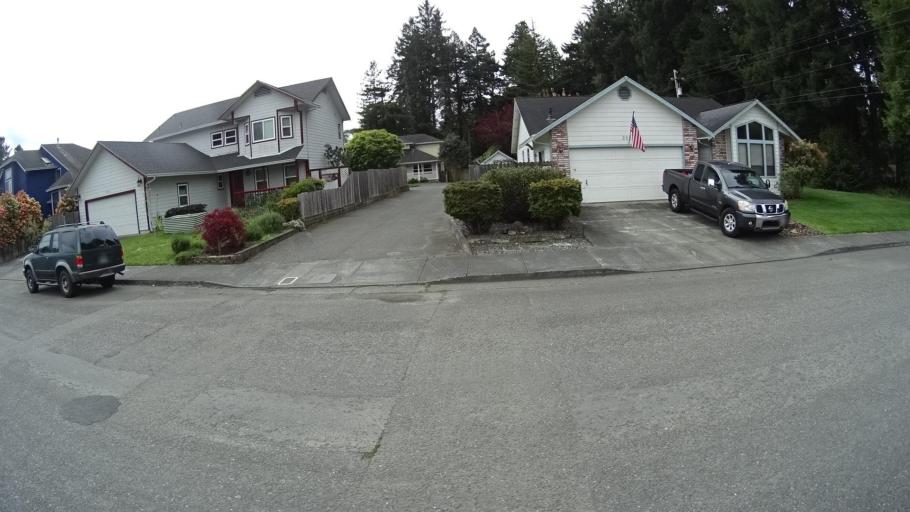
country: US
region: California
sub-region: Humboldt County
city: Cutten
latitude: 40.7699
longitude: -124.1474
